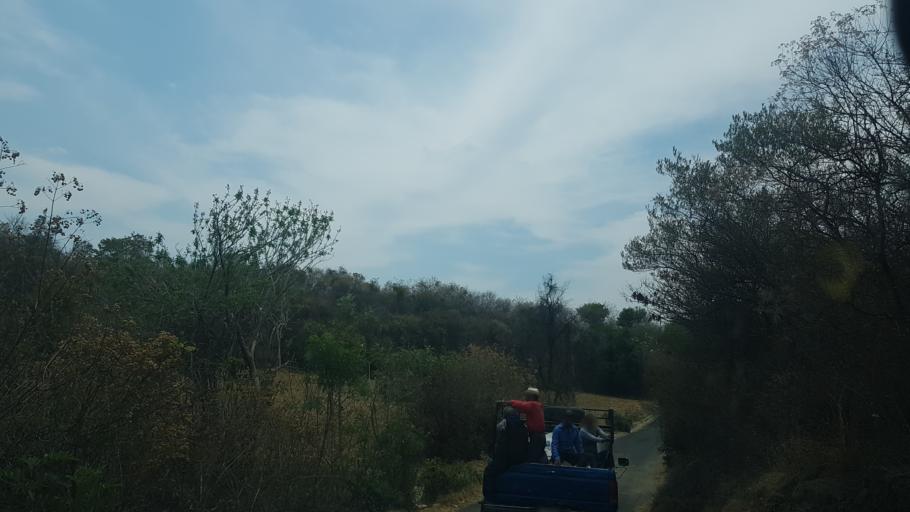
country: MX
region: Puebla
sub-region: Atzitzihuacan
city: Santiago Atzitzihuacan
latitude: 18.8471
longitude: -98.6086
